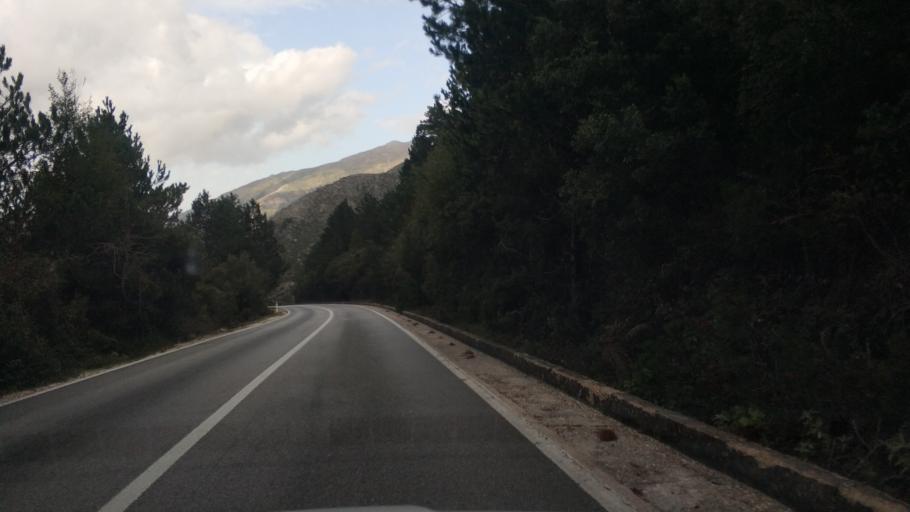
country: AL
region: Vlore
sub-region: Rrethi i Vlores
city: Brataj
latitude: 40.2266
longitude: 19.5782
